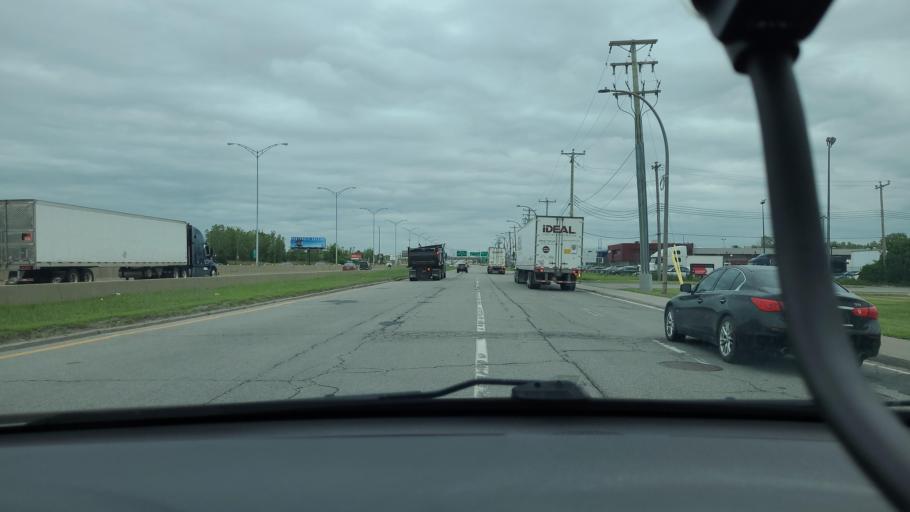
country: CA
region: Quebec
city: Montreal-Est
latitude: 45.6543
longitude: -73.5233
